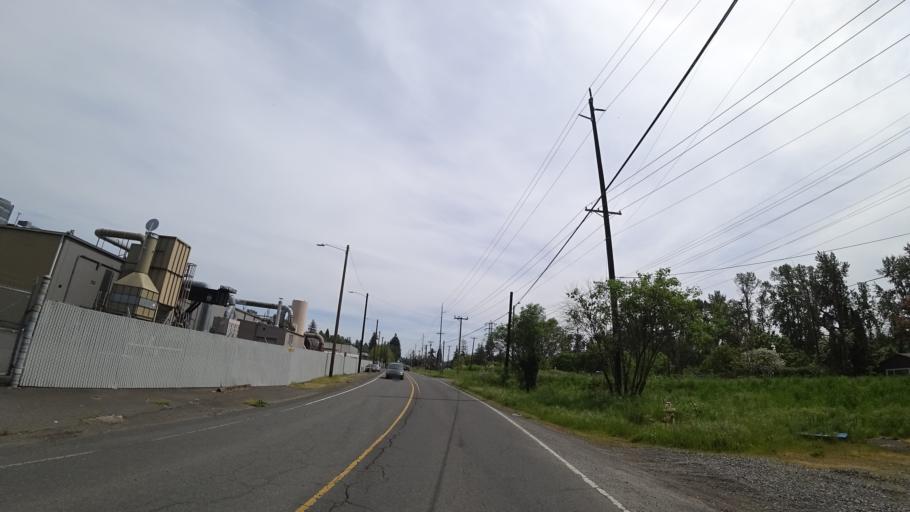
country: US
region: Oregon
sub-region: Clackamas County
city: Milwaukie
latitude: 45.4613
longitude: -122.6151
